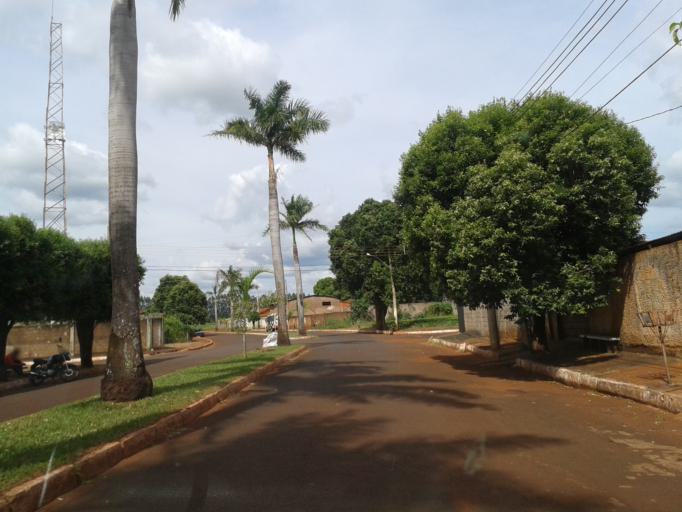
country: BR
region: Minas Gerais
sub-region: Centralina
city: Centralina
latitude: -18.5931
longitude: -49.1978
